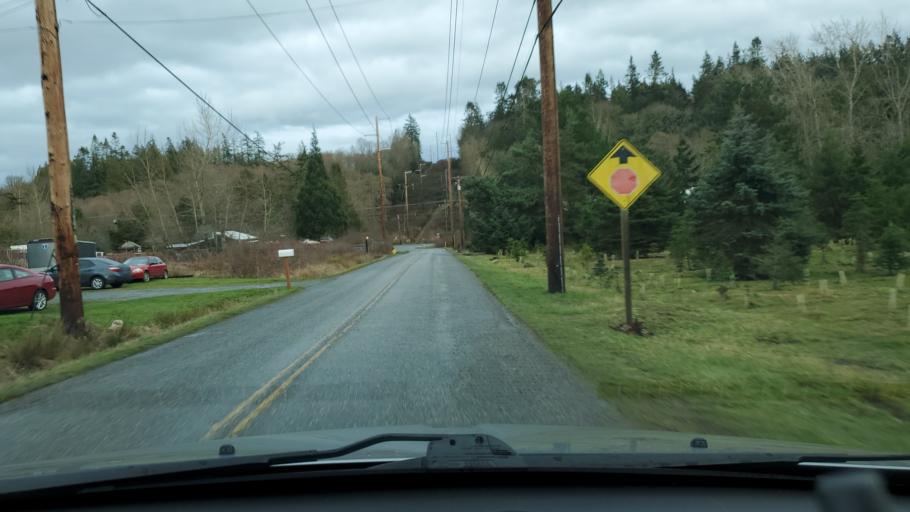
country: US
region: Washington
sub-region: Skagit County
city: Anacortes
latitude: 48.4583
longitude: -122.5465
